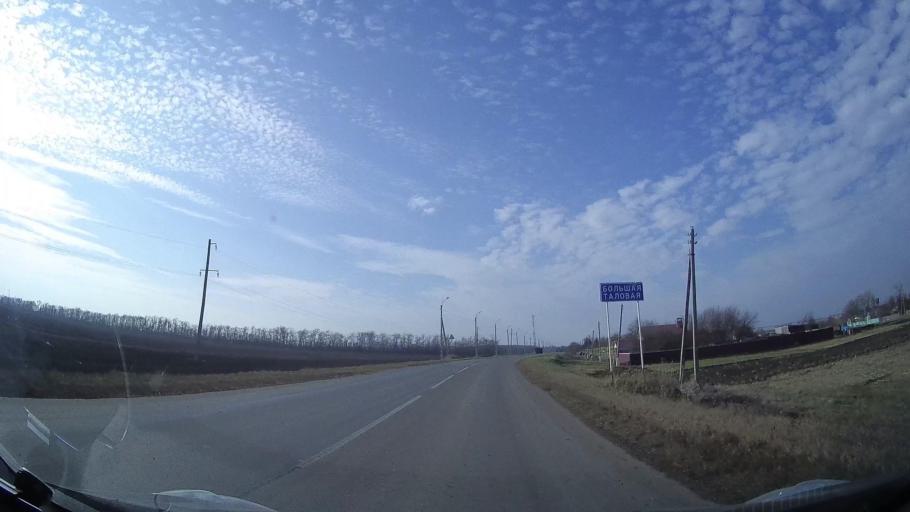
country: RU
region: Rostov
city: Veselyy
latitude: 46.9684
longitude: 40.6303
